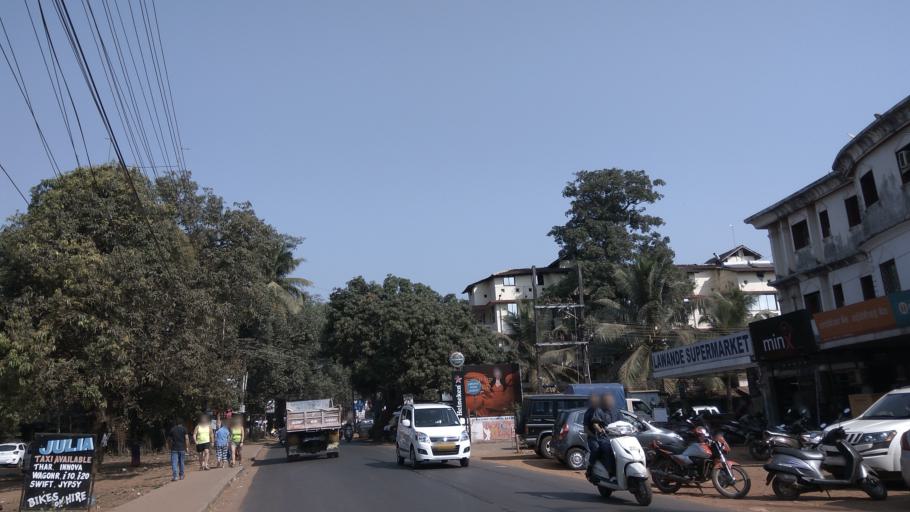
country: IN
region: Goa
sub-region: North Goa
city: Candolim
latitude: 15.5239
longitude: 73.7665
